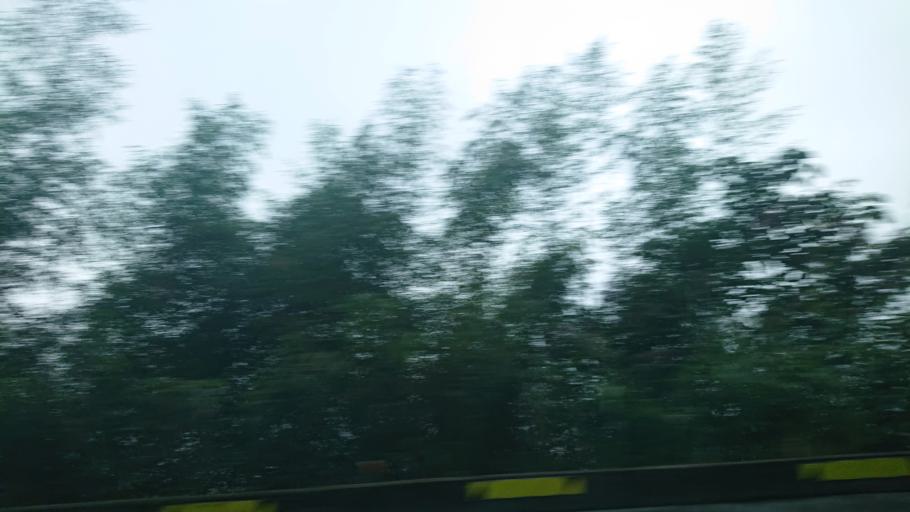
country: TW
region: Taiwan
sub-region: Chiayi
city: Jiayi Shi
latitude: 23.4664
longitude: 120.7178
